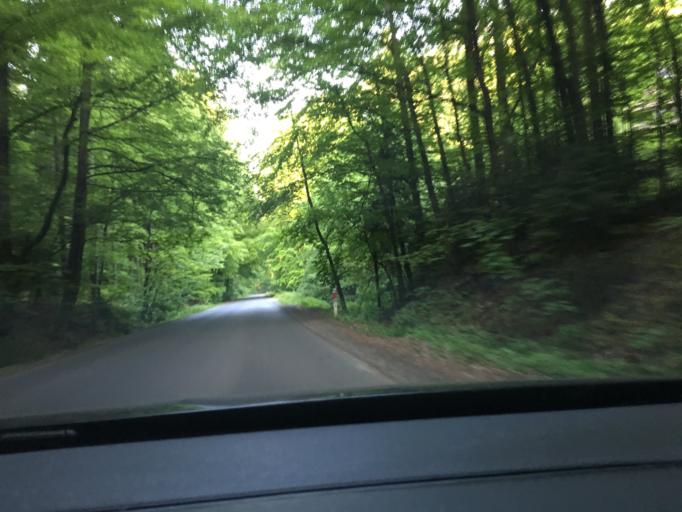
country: PL
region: Lesser Poland Voivodeship
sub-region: Powiat krakowski
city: Skala
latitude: 50.2115
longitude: 19.8190
